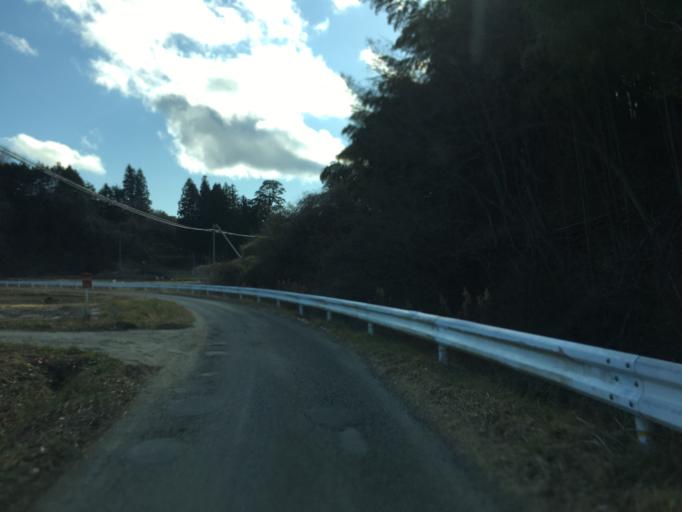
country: JP
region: Fukushima
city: Funehikimachi-funehiki
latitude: 37.4206
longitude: 140.5539
